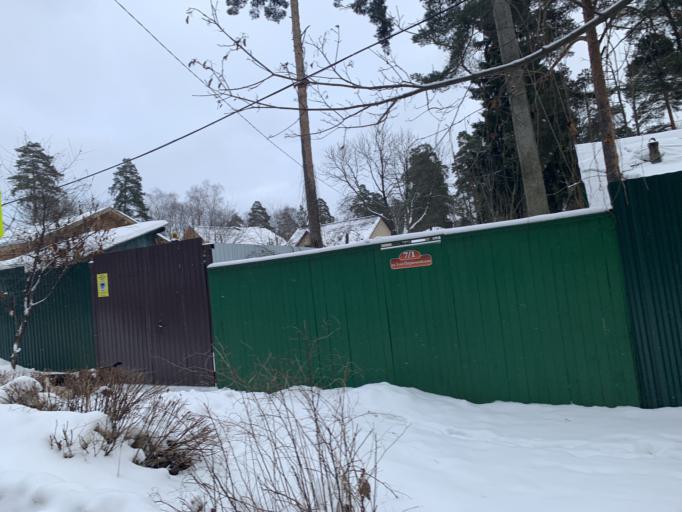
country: RU
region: Moskovskaya
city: Mamontovka
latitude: 55.9908
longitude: 37.8344
